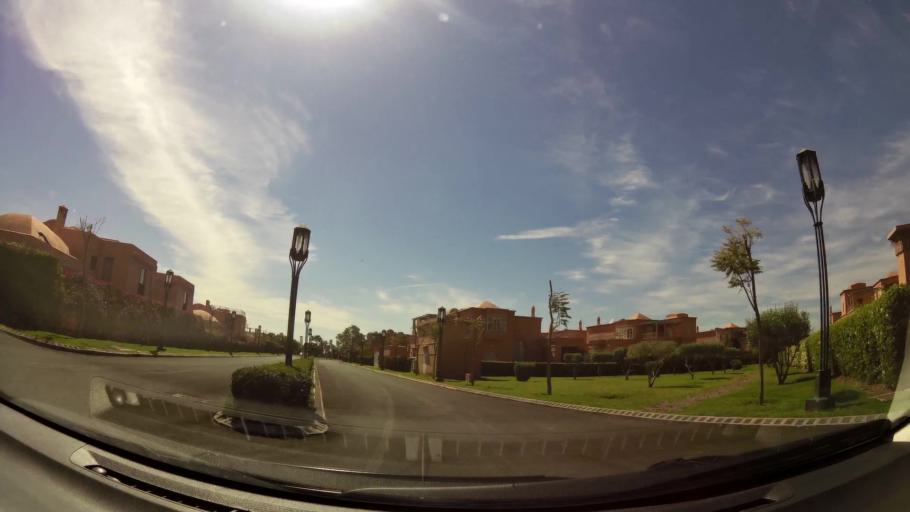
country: MA
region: Marrakech-Tensift-Al Haouz
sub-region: Marrakech
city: Marrakesh
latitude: 31.6194
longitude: -7.9336
